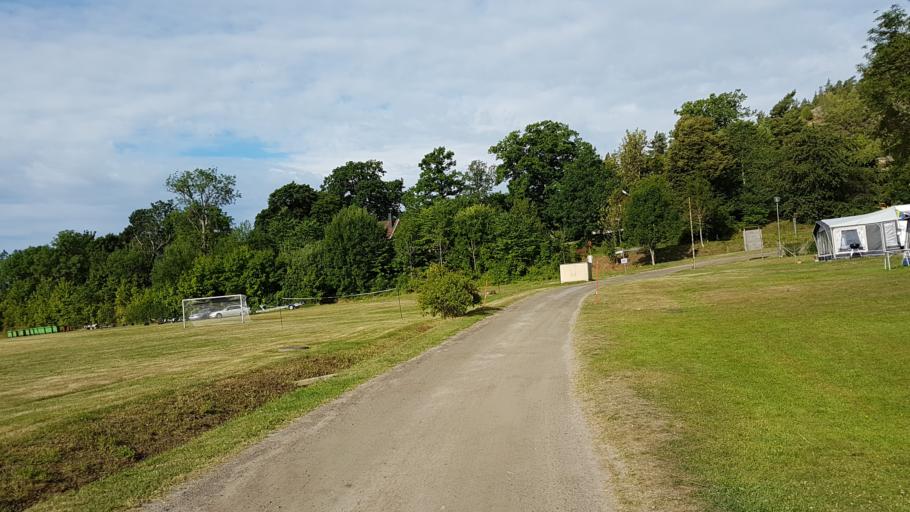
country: SE
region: OEstergoetland
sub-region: Valdemarsviks Kommun
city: Gusum
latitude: 58.4457
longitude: 16.5988
